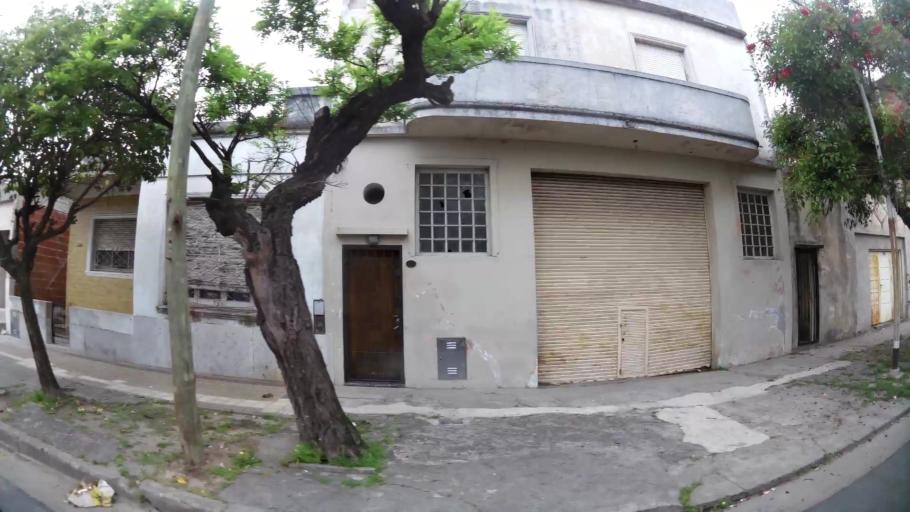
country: AR
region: Buenos Aires
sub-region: Partido de Avellaneda
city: Avellaneda
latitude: -34.6474
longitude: -58.3491
